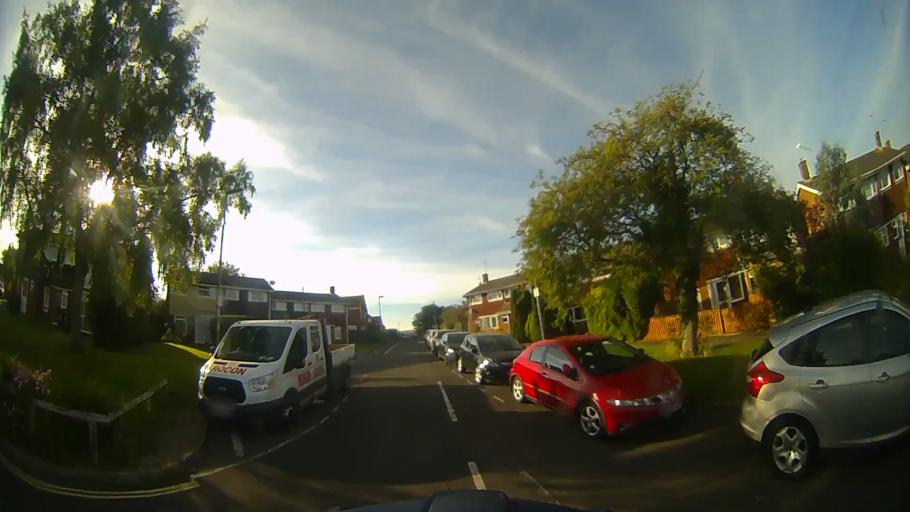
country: GB
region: England
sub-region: Hampshire
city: Basingstoke
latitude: 51.2615
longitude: -1.0978
